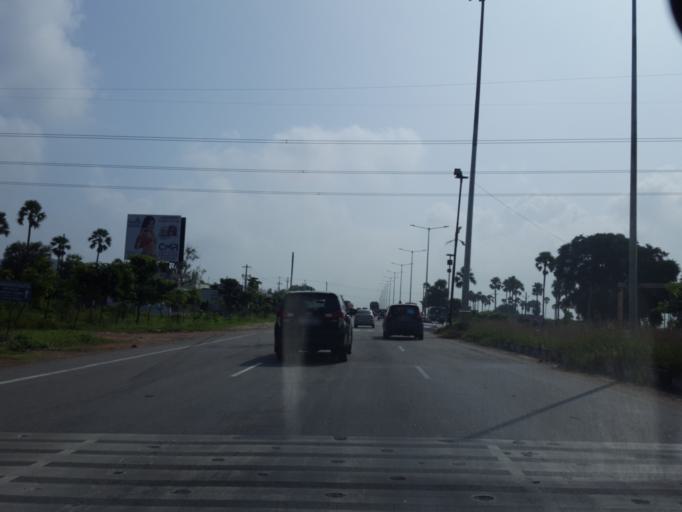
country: IN
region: Telangana
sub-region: Rangareddi
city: Ghatkesar
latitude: 17.3068
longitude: 78.7149
